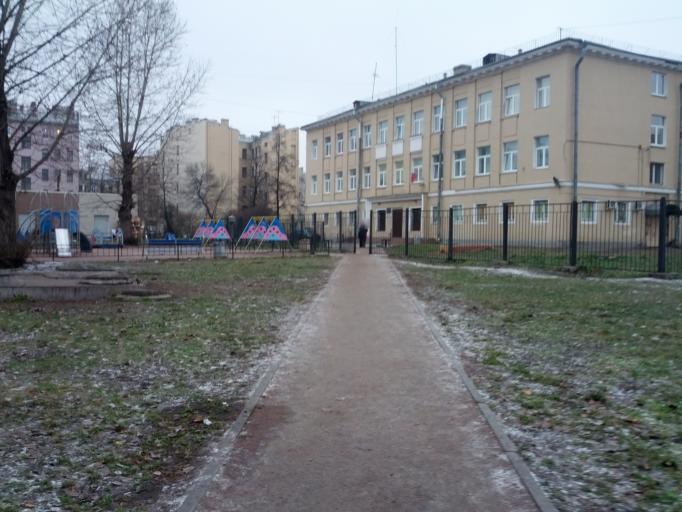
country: RU
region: St.-Petersburg
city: Centralniy
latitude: 59.9121
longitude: 30.3517
